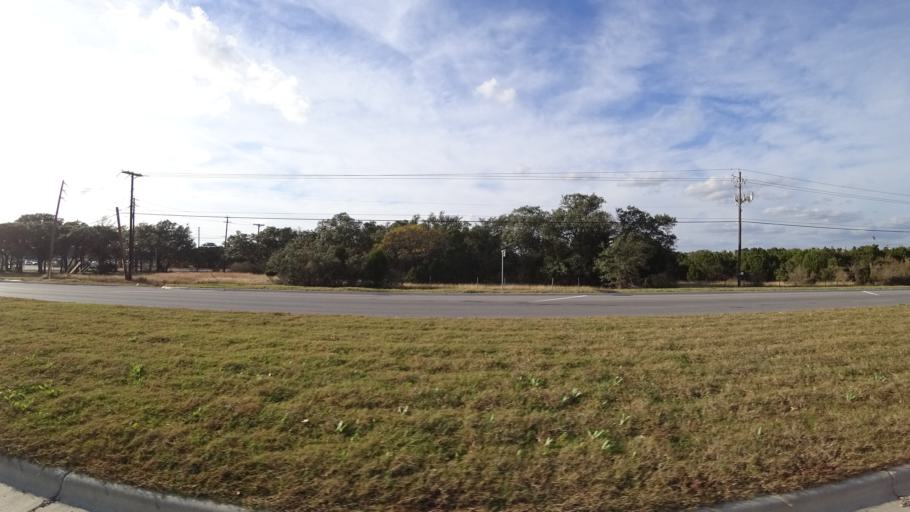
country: US
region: Texas
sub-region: Williamson County
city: Brushy Creek
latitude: 30.5017
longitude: -97.7198
